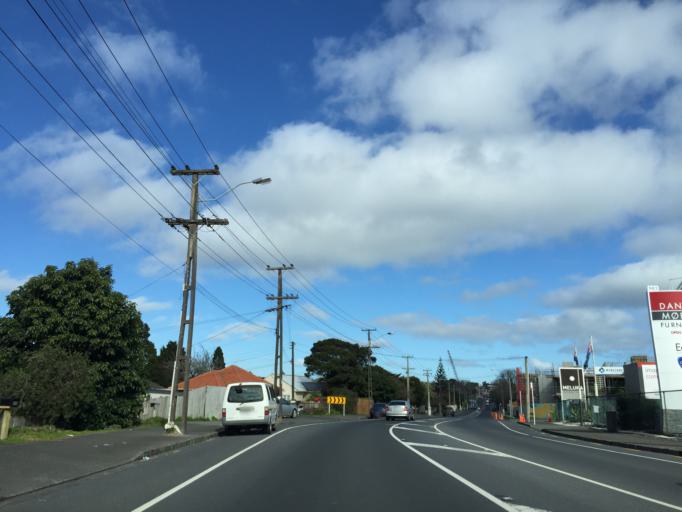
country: NZ
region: Auckland
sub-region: Auckland
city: Auckland
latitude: -36.9027
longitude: 174.7595
